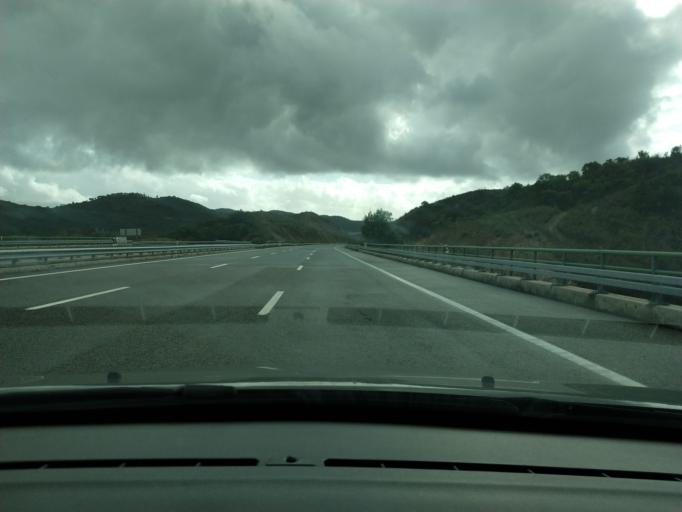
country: PT
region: Faro
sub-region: Silves
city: Sao Bartolomeu de Messines
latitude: 37.4264
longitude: -8.2403
